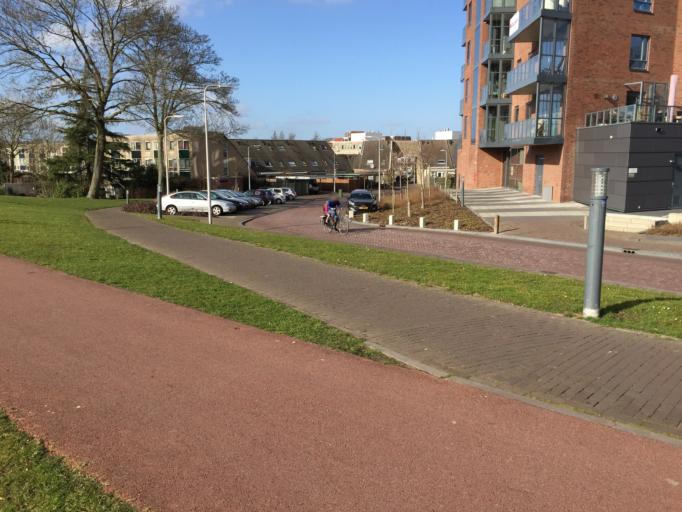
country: NL
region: South Holland
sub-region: Gemeente Krimpen aan den IJssel
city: Krimpen aan den IJssel
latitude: 51.9659
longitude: 4.6171
